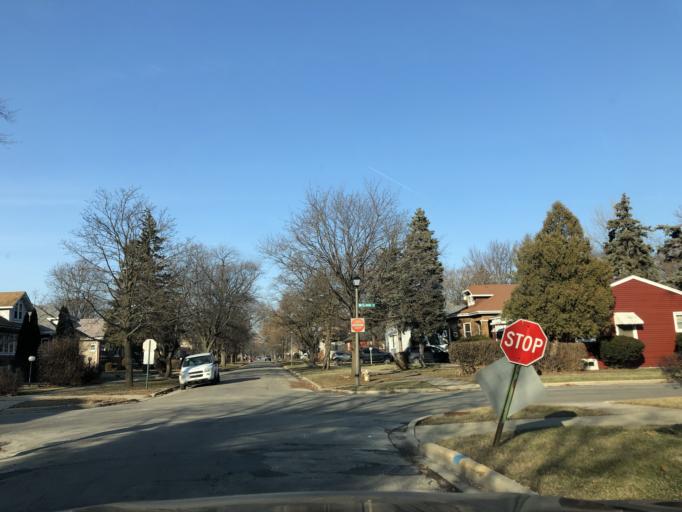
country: US
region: Illinois
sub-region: Cook County
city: Maywood
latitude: 41.8661
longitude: -87.8358
